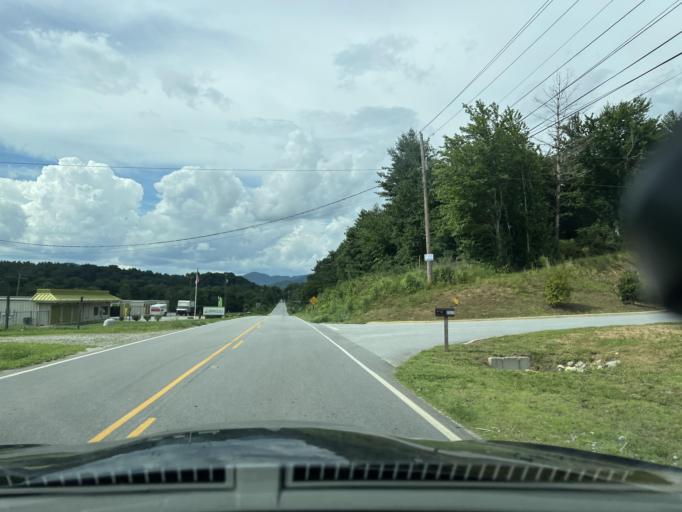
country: US
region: North Carolina
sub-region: Henderson County
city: Hoopers Creek
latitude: 35.4425
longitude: -82.4758
